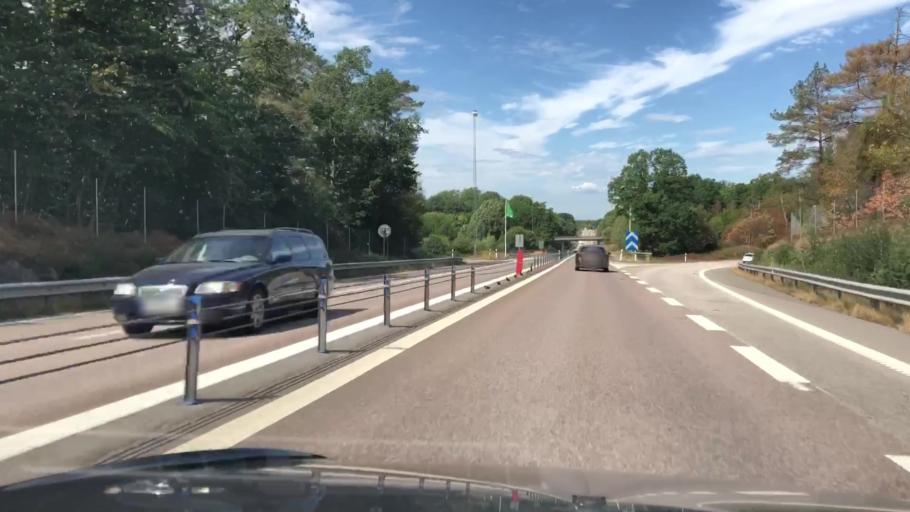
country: SE
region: Blekinge
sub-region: Ronneby Kommun
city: Ronneby
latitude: 56.2202
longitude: 15.2842
